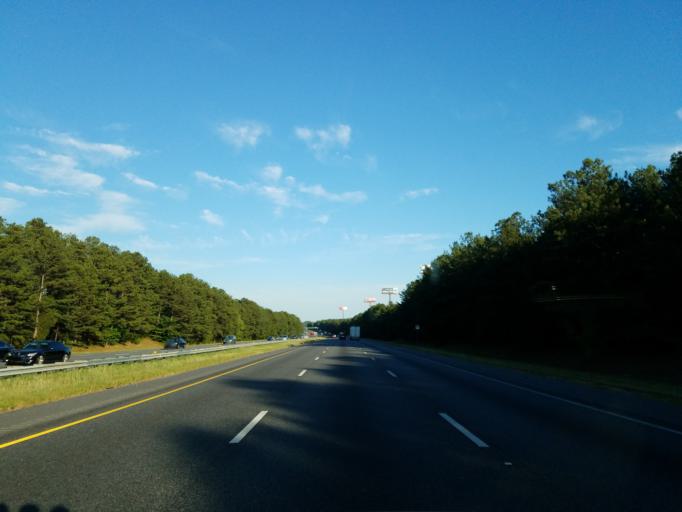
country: US
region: Georgia
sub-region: Bartow County
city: Adairsville
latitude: 34.3438
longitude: -84.8747
